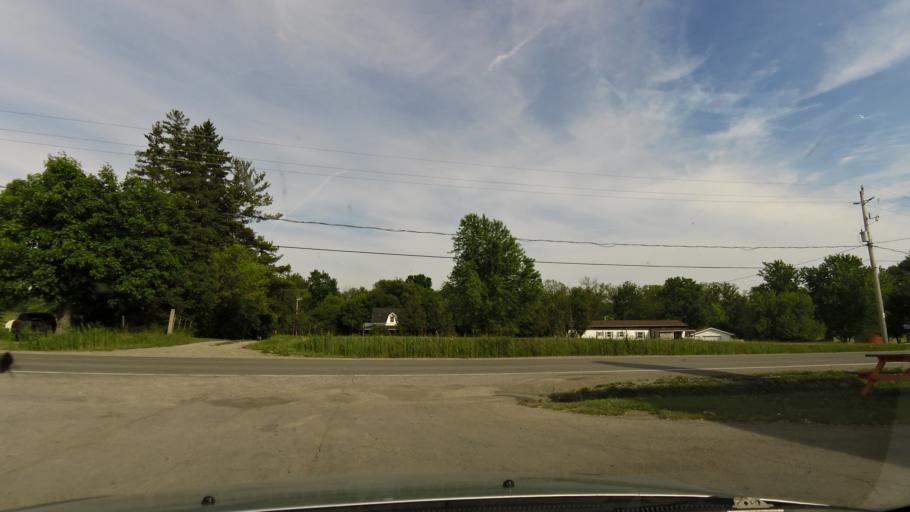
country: CA
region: Ontario
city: Brantford
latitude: 43.0819
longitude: -80.1097
